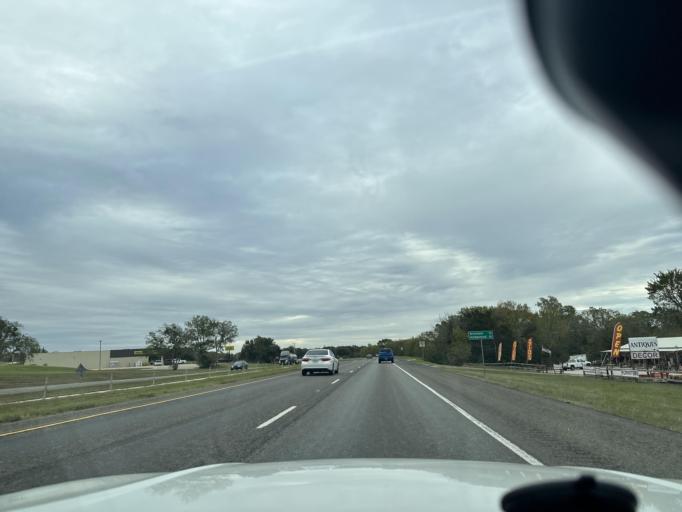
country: US
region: Texas
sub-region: Burleson County
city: Somerville
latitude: 30.1751
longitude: -96.6005
